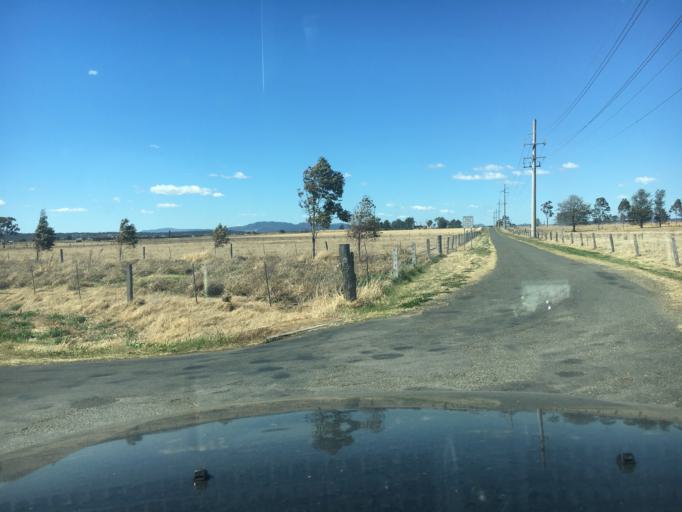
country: AU
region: New South Wales
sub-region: Singleton
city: Singleton
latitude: -32.5897
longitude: 151.1662
